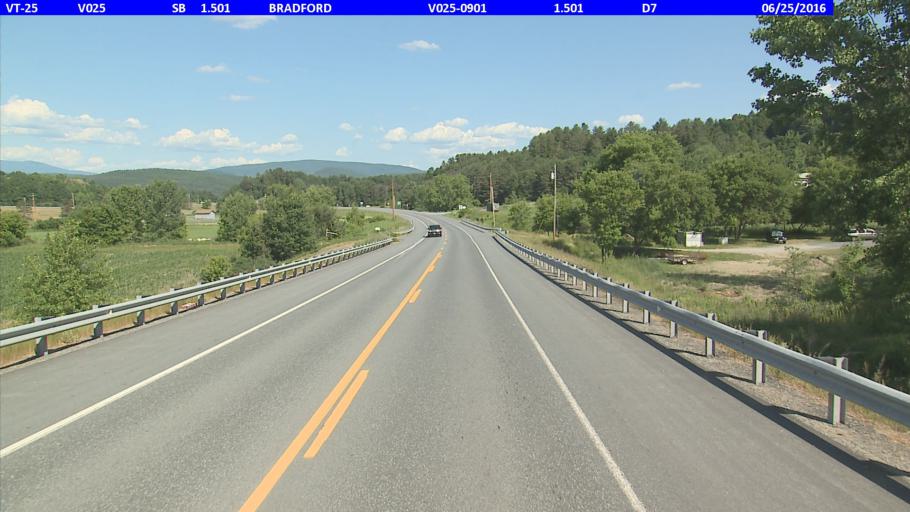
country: US
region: New Hampshire
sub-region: Grafton County
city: Orford
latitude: 43.9849
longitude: -72.1387
